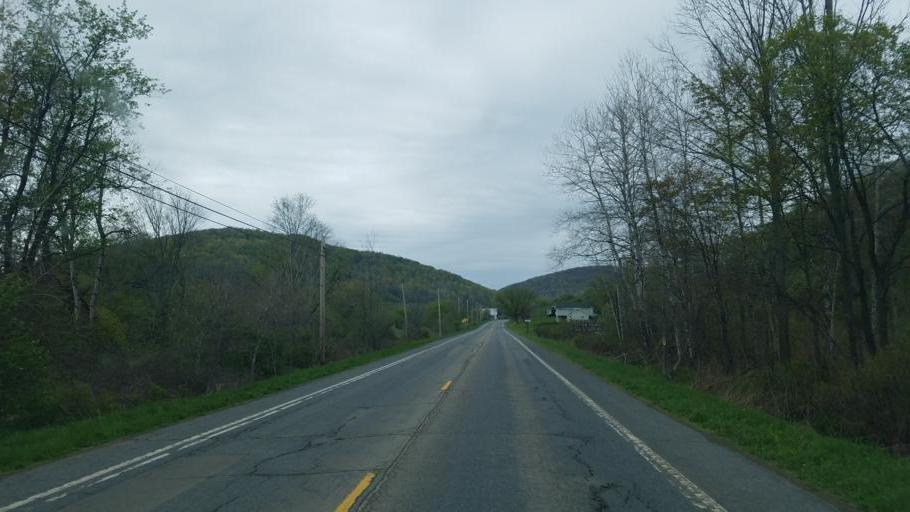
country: US
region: Pennsylvania
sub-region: Tioga County
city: Westfield
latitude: 41.9163
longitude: -77.6154
